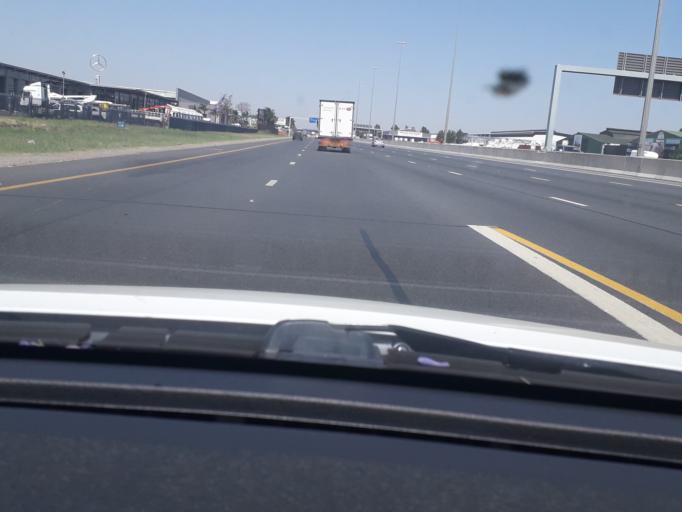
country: ZA
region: Gauteng
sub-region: Ekurhuleni Metropolitan Municipality
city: Boksburg
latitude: -26.1754
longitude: 28.2266
